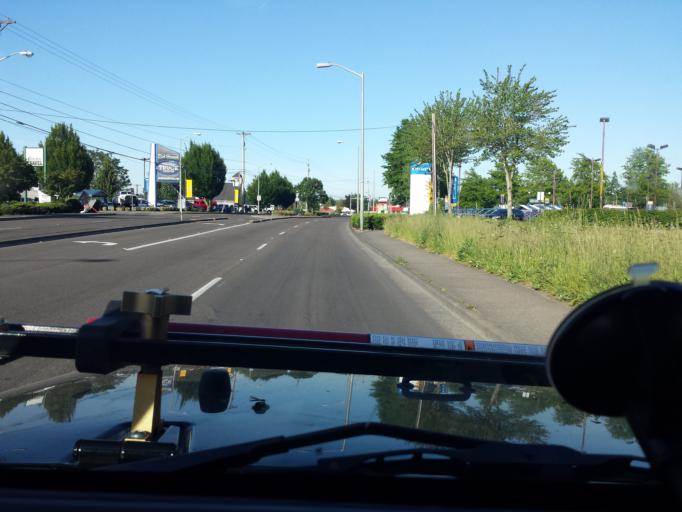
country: US
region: Washington
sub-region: Clark County
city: Walnut Grove
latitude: 45.6461
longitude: -122.5954
